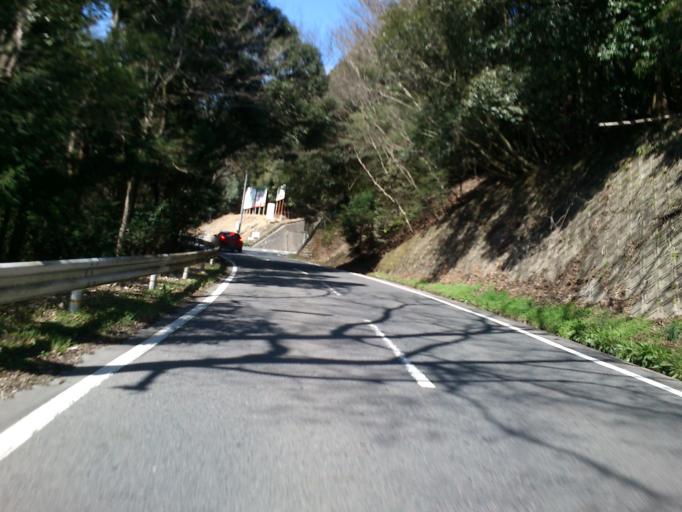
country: JP
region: Kyoto
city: Uji
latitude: 34.9172
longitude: 135.8589
